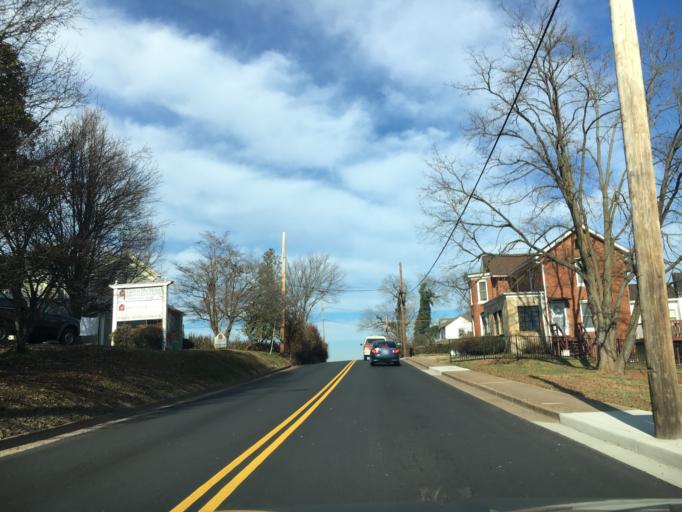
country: US
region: Virginia
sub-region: Culpeper County
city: Culpeper
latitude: 38.4653
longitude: -77.9978
